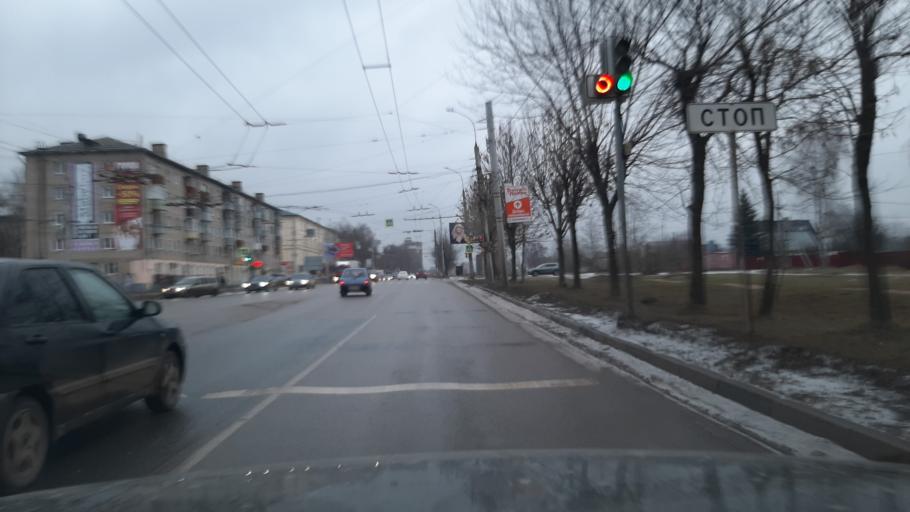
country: RU
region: Ivanovo
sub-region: Gorod Ivanovo
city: Ivanovo
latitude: 56.9700
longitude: 41.0153
